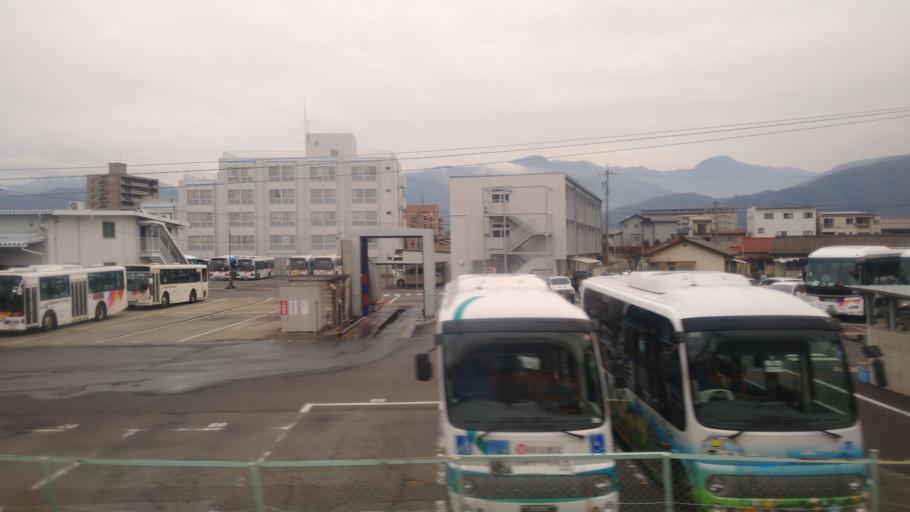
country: JP
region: Nagano
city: Matsumoto
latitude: 36.2217
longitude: 137.9694
